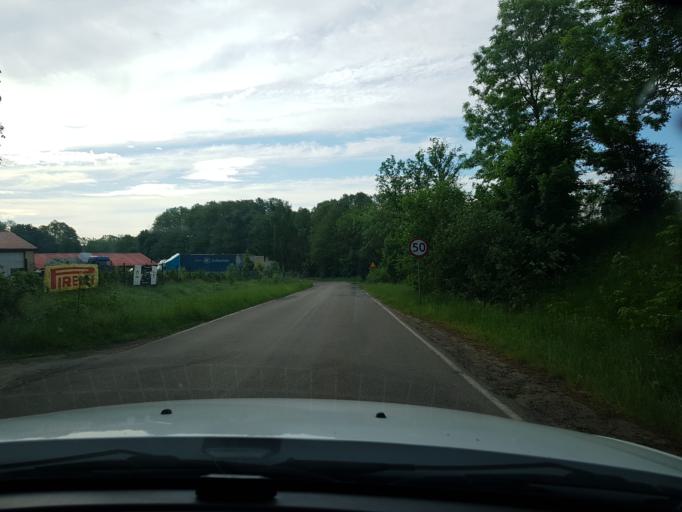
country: PL
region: West Pomeranian Voivodeship
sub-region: Powiat stargardzki
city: Chociwel
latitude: 53.4693
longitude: 15.3555
